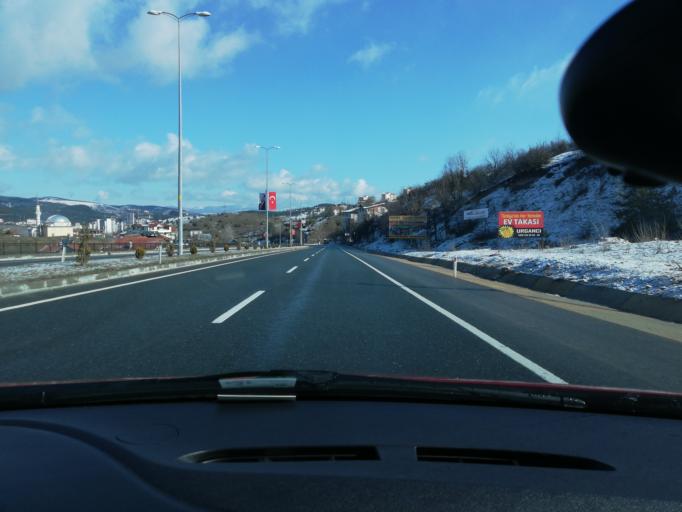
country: TR
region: Kastamonu
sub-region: Cide
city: Kastamonu
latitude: 41.3419
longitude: 33.7664
